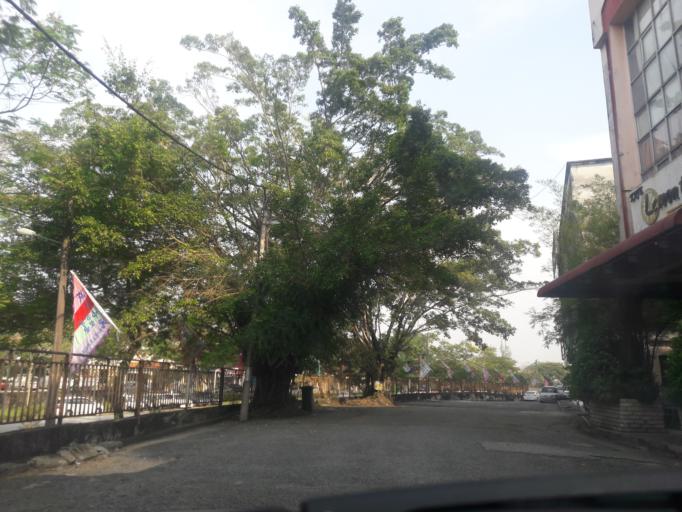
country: MY
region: Kedah
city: Kulim
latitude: 5.3697
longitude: 100.5426
